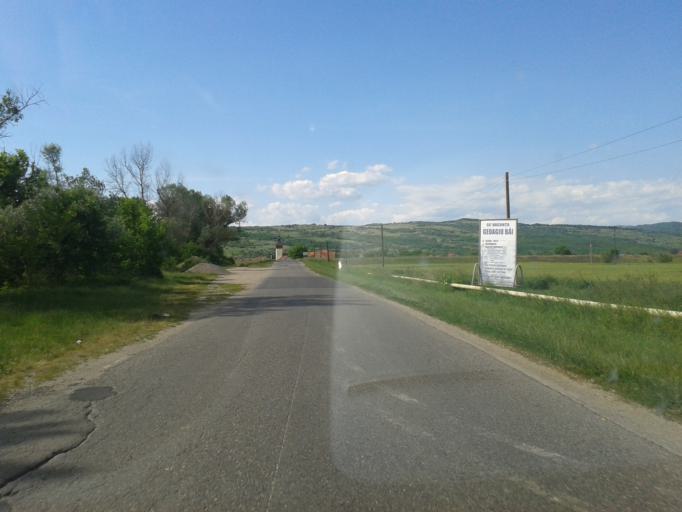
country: RO
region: Hunedoara
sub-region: Comuna Geoagiu
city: Geoagiu
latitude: 45.8971
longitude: 23.2258
